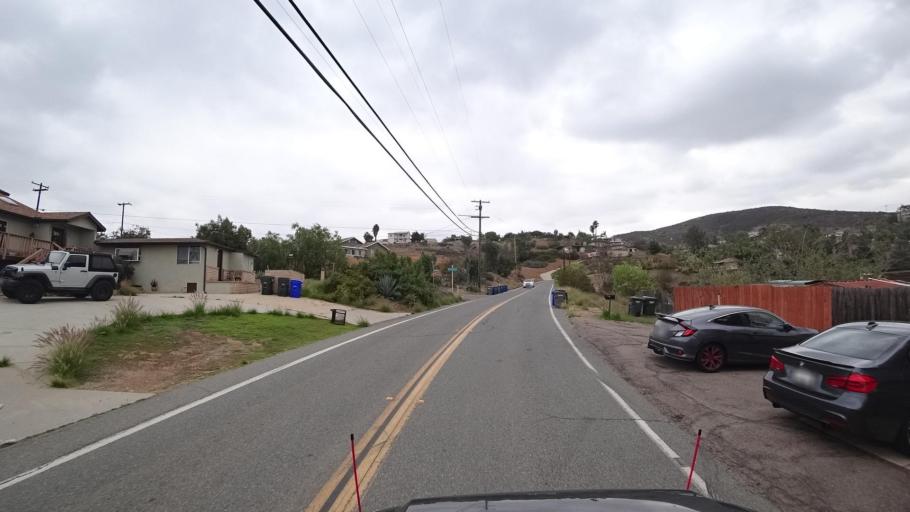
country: US
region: California
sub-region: San Diego County
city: Spring Valley
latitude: 32.7317
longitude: -116.9989
